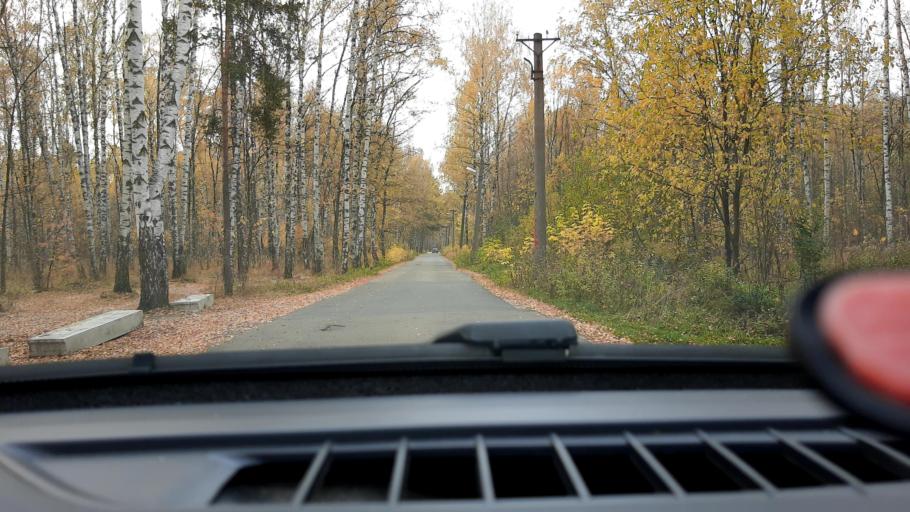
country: RU
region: Nizjnij Novgorod
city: Gorbatovka
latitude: 56.2870
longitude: 43.8300
